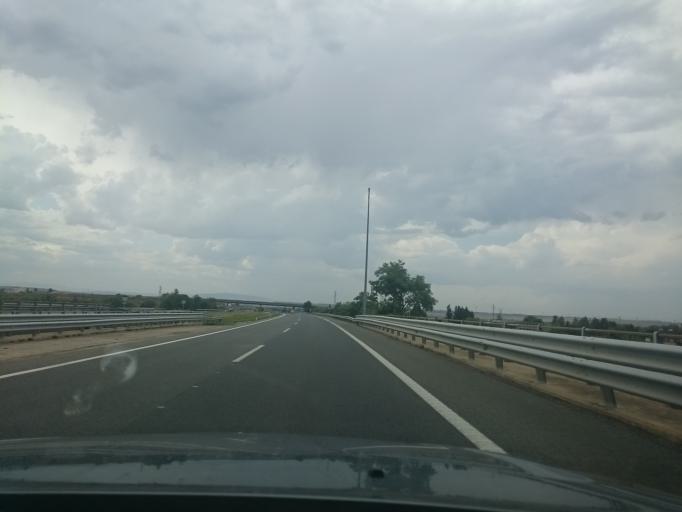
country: ES
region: Navarre
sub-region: Provincia de Navarra
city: Murchante
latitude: 42.0305
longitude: -1.6318
